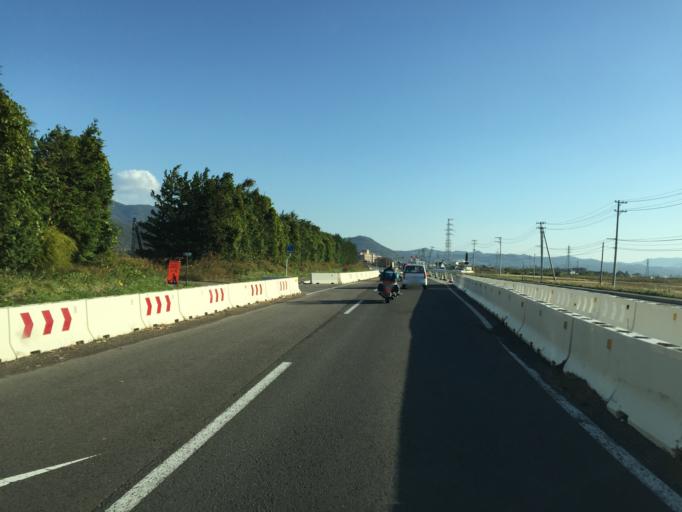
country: JP
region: Fukushima
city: Hobaramachi
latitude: 37.8654
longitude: 140.5320
